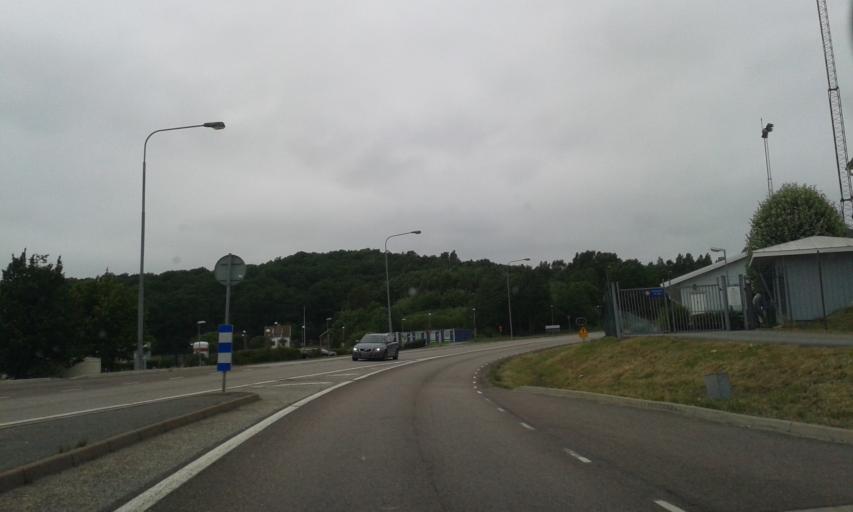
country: SE
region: Vaestra Goetaland
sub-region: Kungalvs Kommun
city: Kungalv
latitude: 57.8779
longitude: 11.9719
